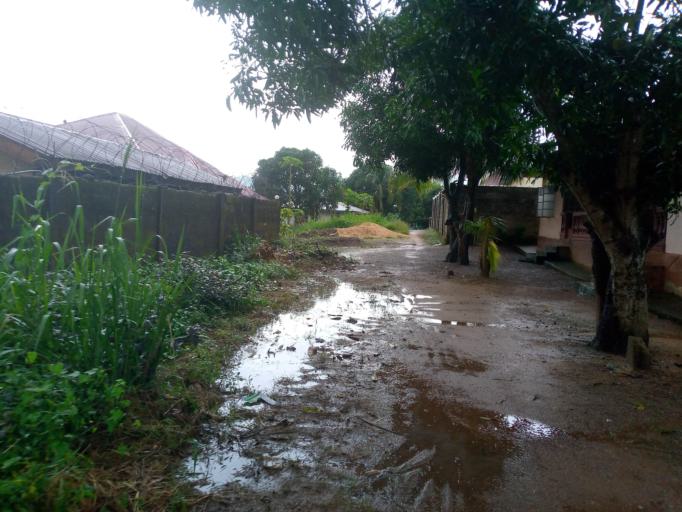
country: SL
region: Eastern Province
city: Kenema
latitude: 7.8792
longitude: -11.1749
